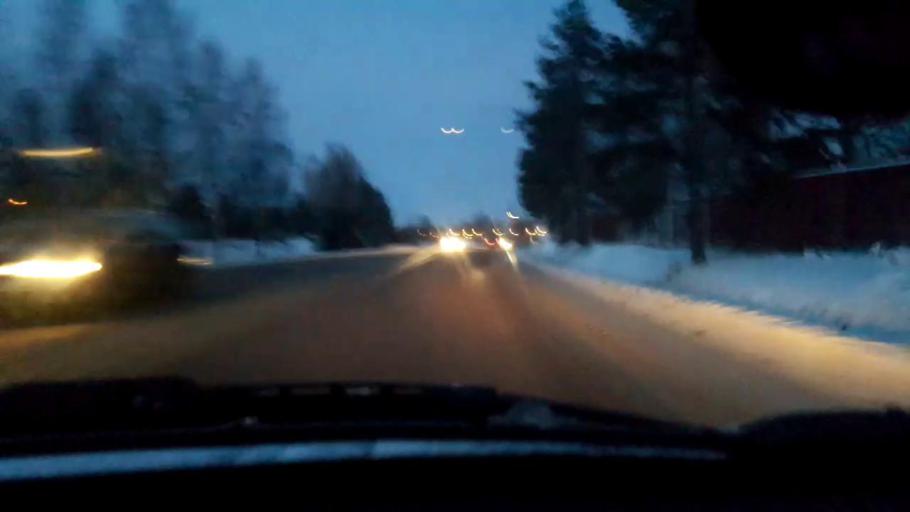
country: SE
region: Dalarna
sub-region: Mora Kommun
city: Mora
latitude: 60.9965
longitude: 14.5324
